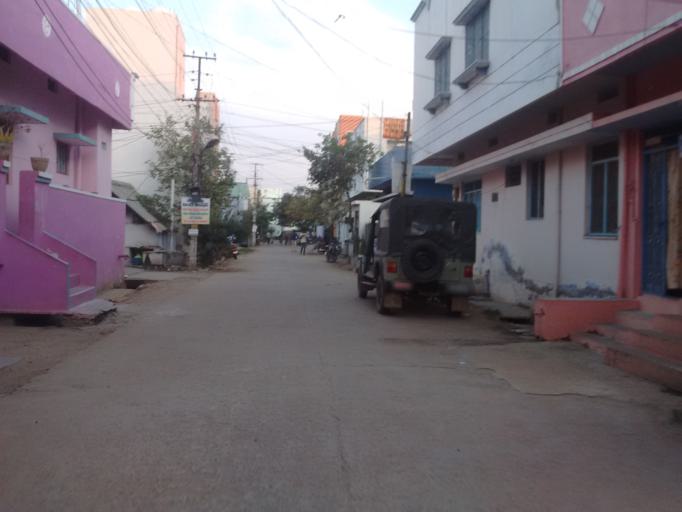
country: IN
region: Telangana
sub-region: Mahbubnagar
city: Alampur
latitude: 15.8122
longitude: 78.0444
